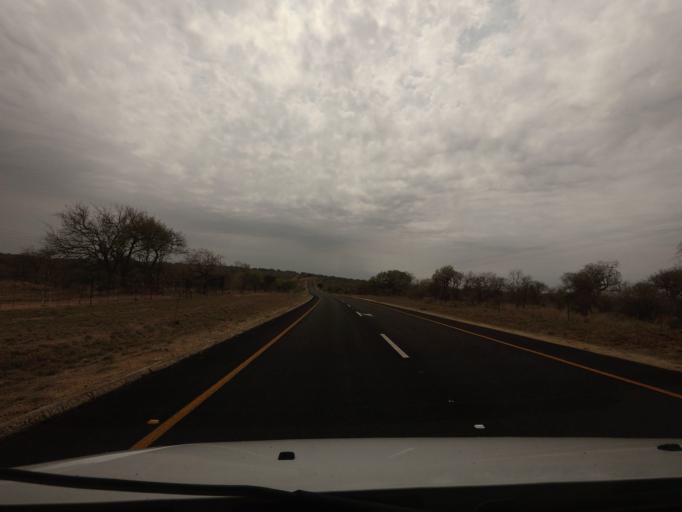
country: ZA
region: Limpopo
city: Thulamahashi
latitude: -24.5587
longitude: 31.1767
